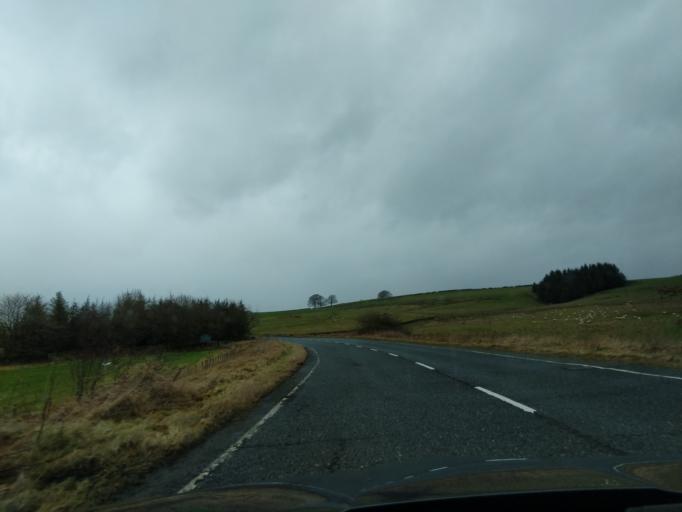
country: GB
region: England
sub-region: Northumberland
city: Otterburn
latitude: 55.2240
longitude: -2.1426
